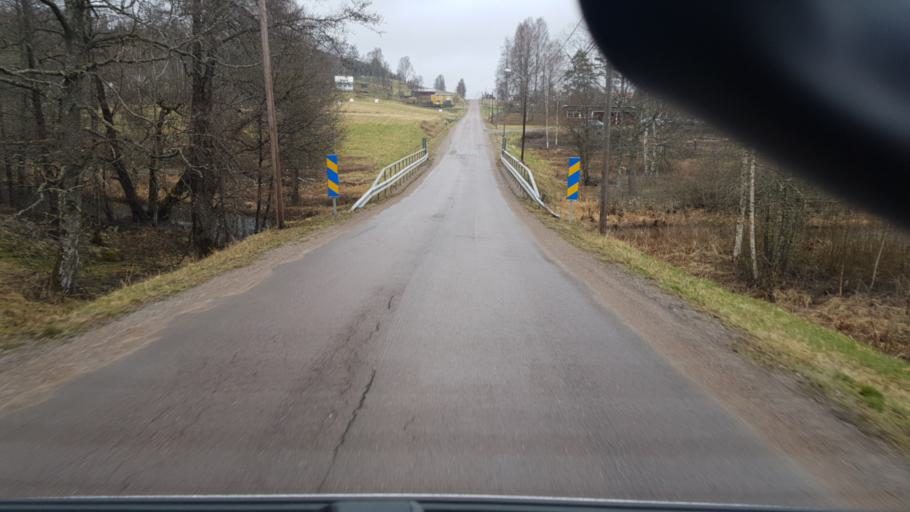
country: SE
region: Vaermland
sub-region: Eda Kommun
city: Charlottenberg
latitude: 59.9317
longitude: 12.5213
